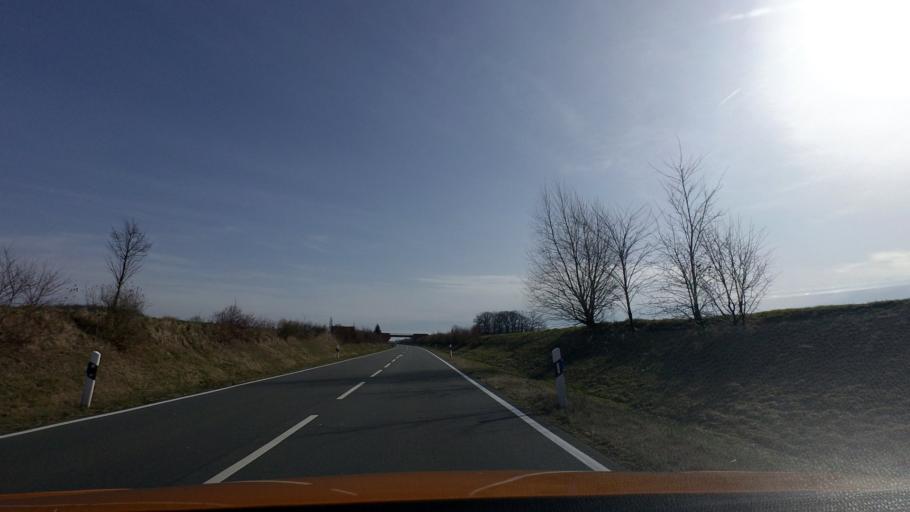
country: DE
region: Lower Saxony
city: Wiedensahl
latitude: 52.3719
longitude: 9.0807
